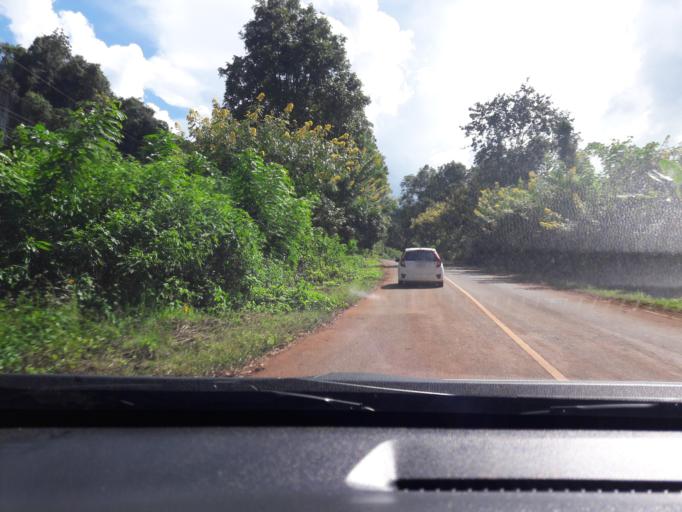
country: TH
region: Mae Hong Son
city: Sop Pong
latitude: 19.5675
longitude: 98.1977
